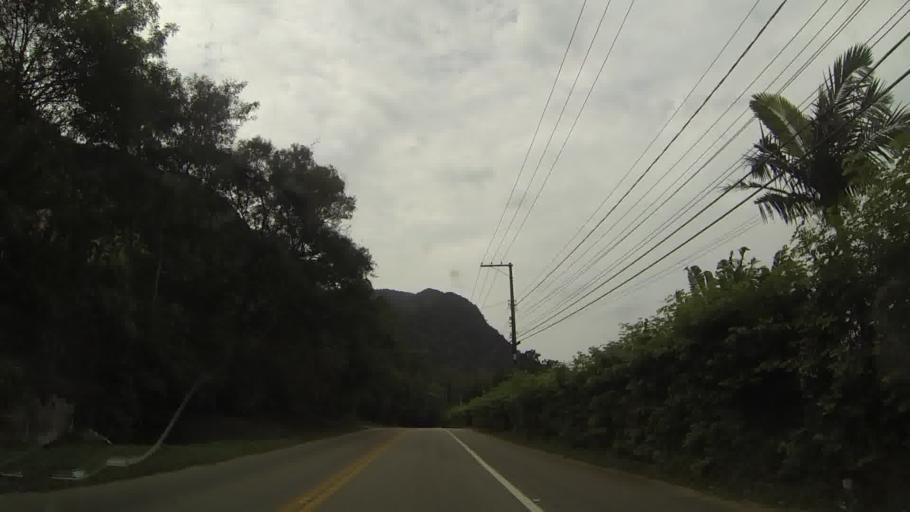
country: BR
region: Sao Paulo
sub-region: Sao Sebastiao
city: Sao Sebastiao
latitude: -23.8302
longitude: -45.5129
